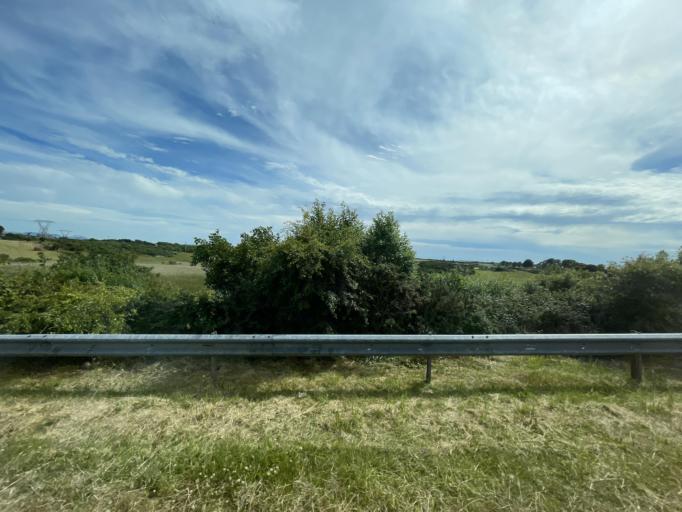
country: GB
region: Wales
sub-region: Anglesey
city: Valley
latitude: 53.2784
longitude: -4.5478
